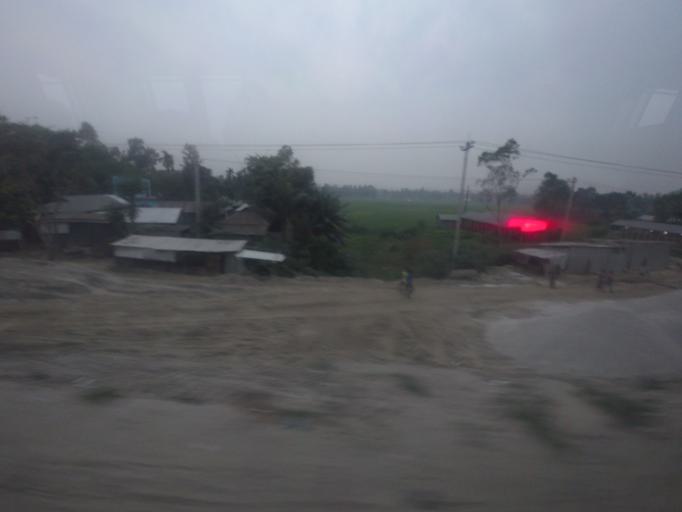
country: BD
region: Dhaka
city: Tangail
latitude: 24.3277
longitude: 89.9249
